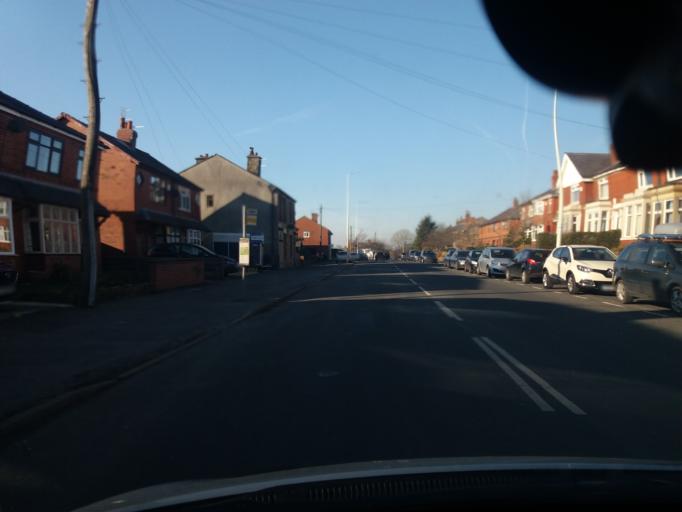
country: GB
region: England
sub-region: Lancashire
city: Adlington
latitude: 53.6230
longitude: -2.6059
